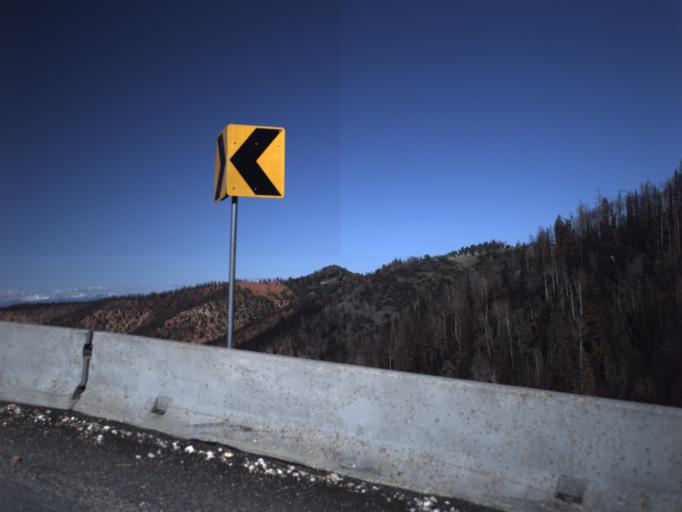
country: US
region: Utah
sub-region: Iron County
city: Parowan
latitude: 37.7162
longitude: -112.8473
